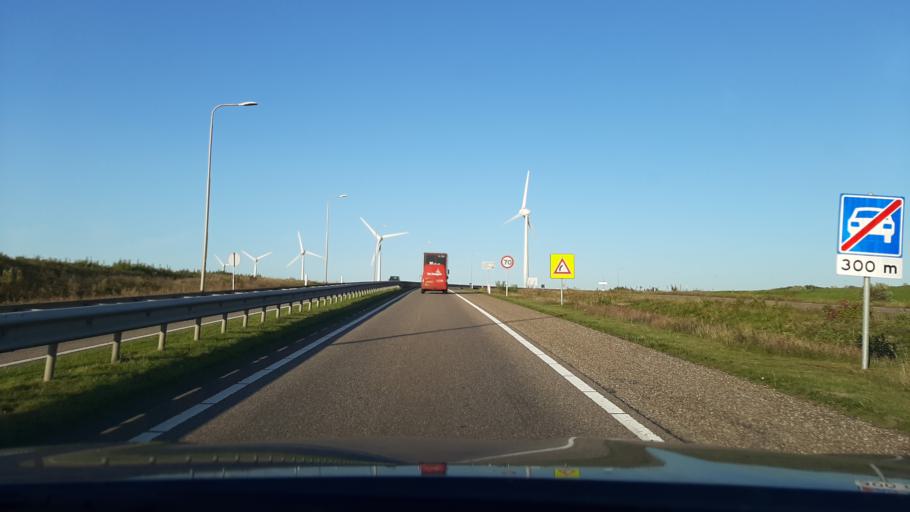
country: NL
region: North Holland
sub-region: Gemeente Enkhuizen
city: Enkhuizen
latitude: 52.6905
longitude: 5.2914
